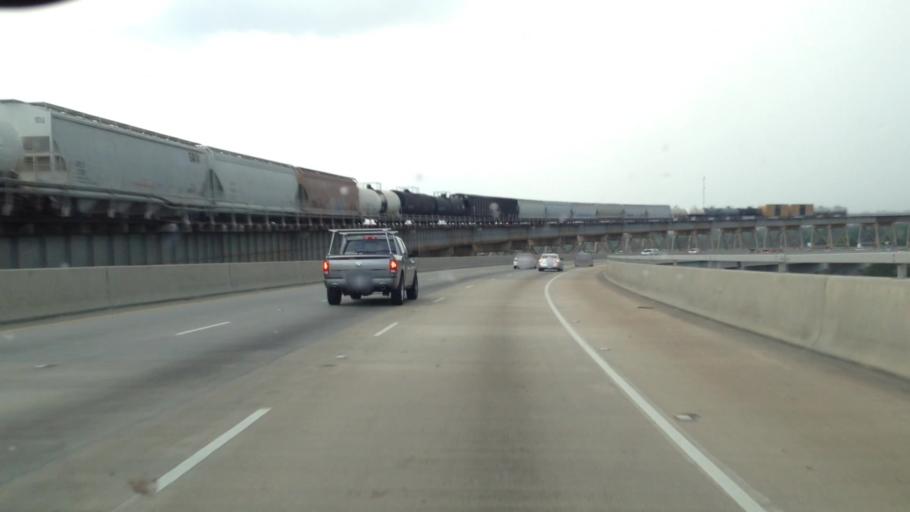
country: US
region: Louisiana
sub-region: Jefferson Parish
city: Bridge City
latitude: 29.9403
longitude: -90.1648
